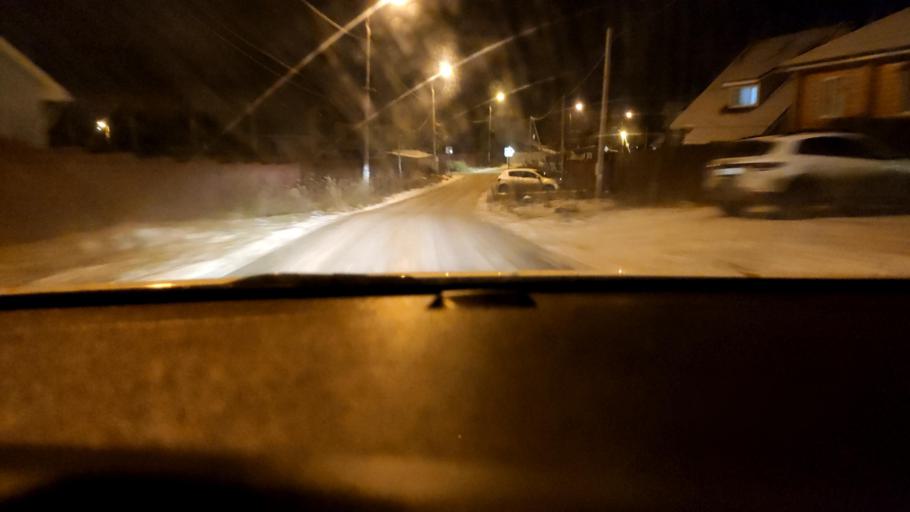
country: RU
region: Tatarstan
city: Osinovo
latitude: 55.8303
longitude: 48.8598
